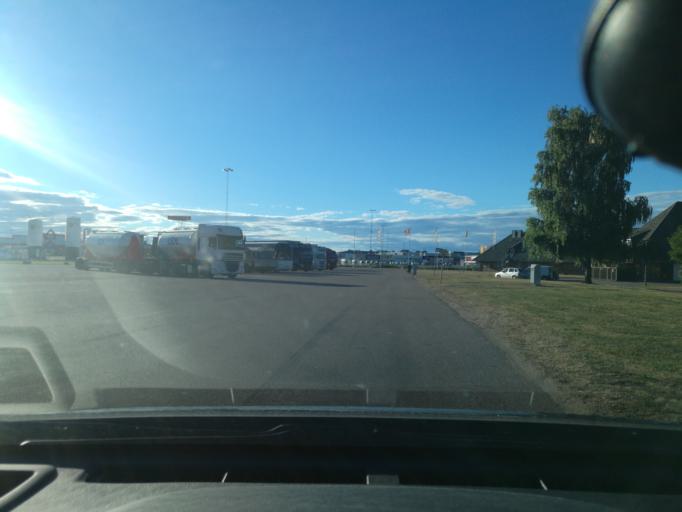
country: SE
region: Kalmar
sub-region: Kalmar Kommun
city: Kalmar
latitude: 56.6828
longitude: 16.3219
